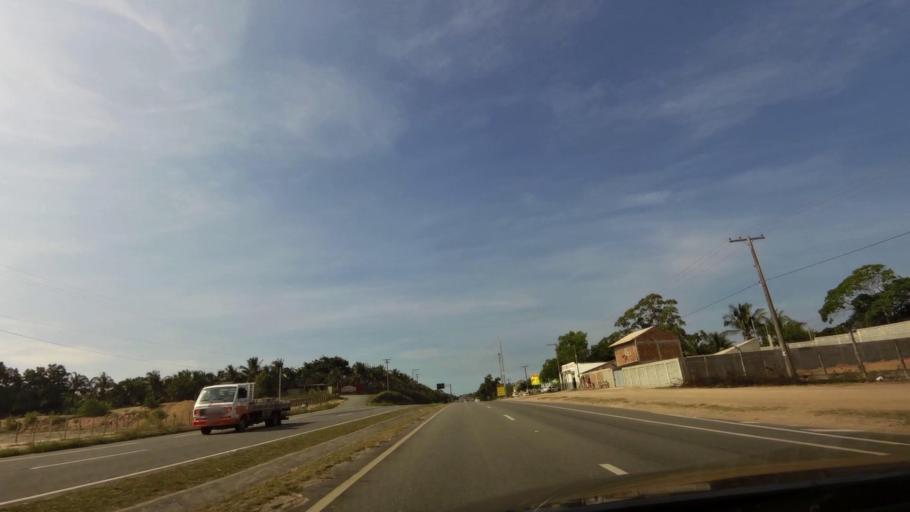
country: BR
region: Espirito Santo
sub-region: Viana
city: Viana
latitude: -20.5242
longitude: -40.3750
